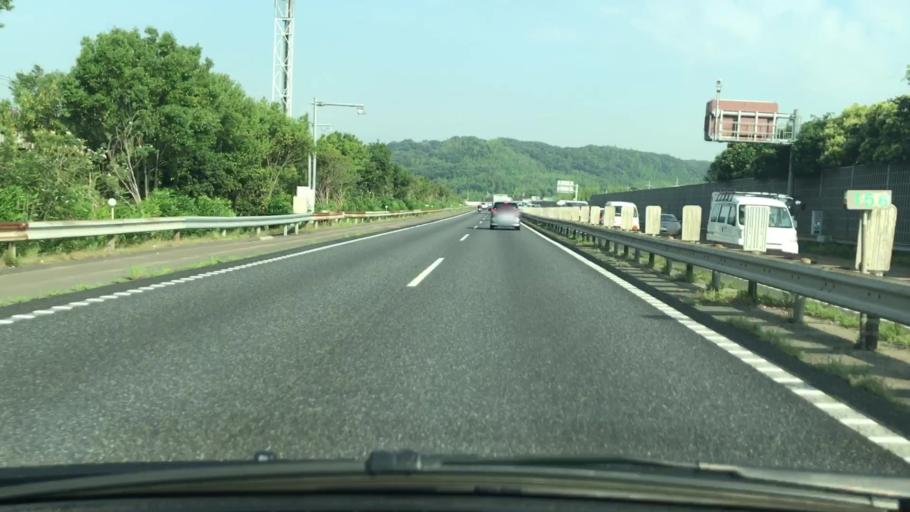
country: JP
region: Hyogo
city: Akashi
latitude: 34.6871
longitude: 134.9758
